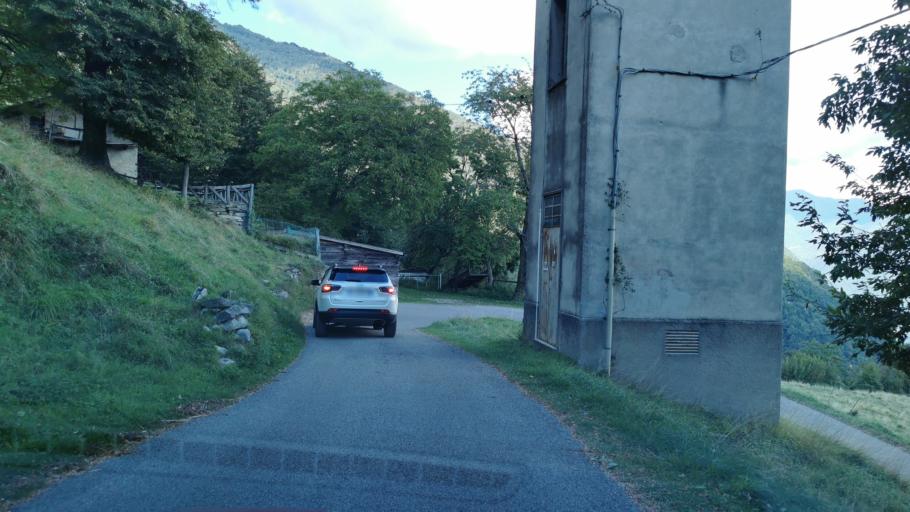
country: IT
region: Lombardy
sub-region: Provincia di Como
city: Moltrasio
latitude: 45.8616
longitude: 9.0868
